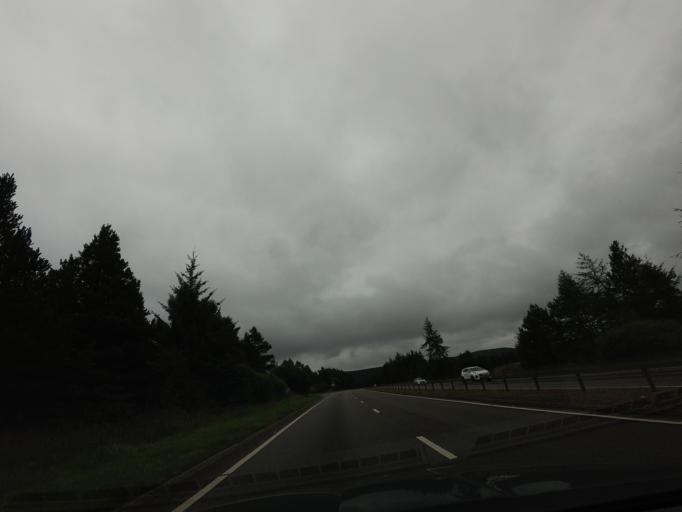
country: GB
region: Scotland
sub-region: Highland
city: Inverness
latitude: 57.3950
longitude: -4.1258
